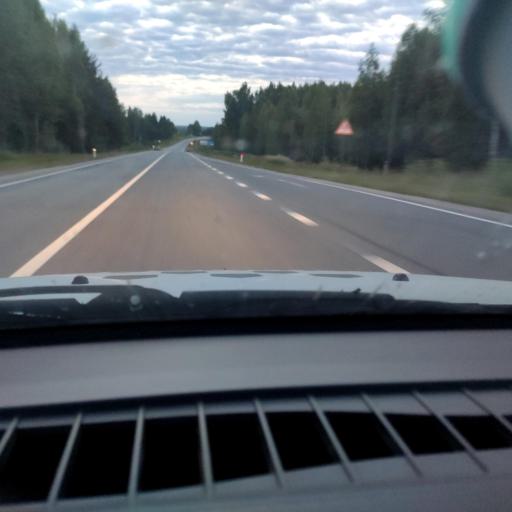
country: RU
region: Kirov
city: Torfyanoy
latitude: 58.7163
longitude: 49.2115
